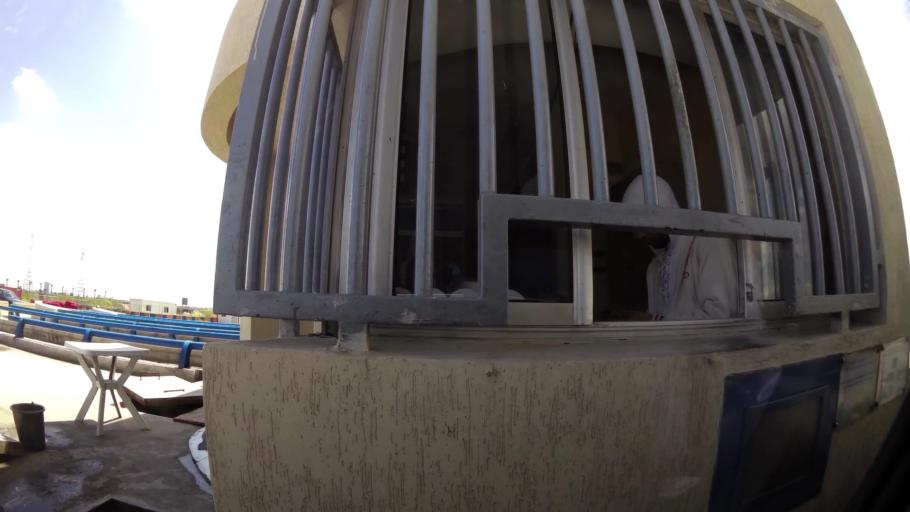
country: MA
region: Grand Casablanca
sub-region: Mediouna
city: Tit Mellil
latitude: 33.5630
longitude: -7.4993
